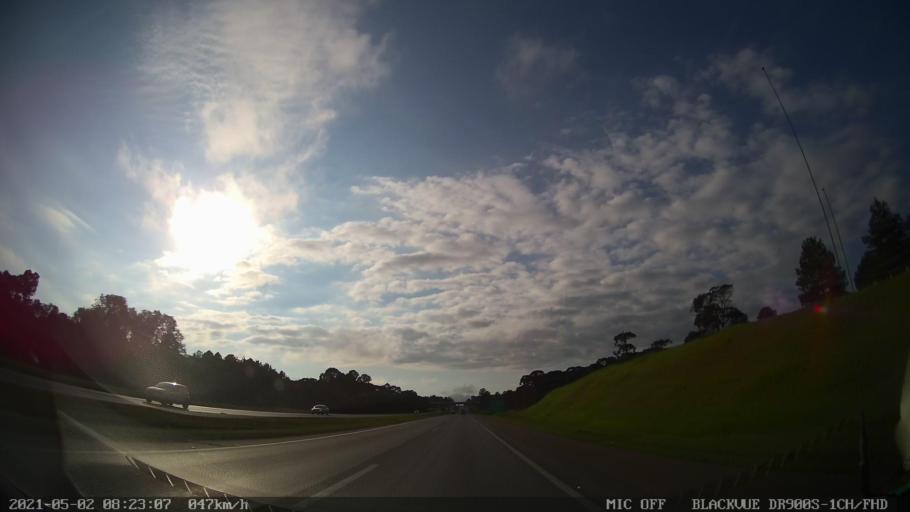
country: BR
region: Parana
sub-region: Sao Jose Dos Pinhais
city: Sao Jose dos Pinhais
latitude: -25.5717
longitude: -49.1971
